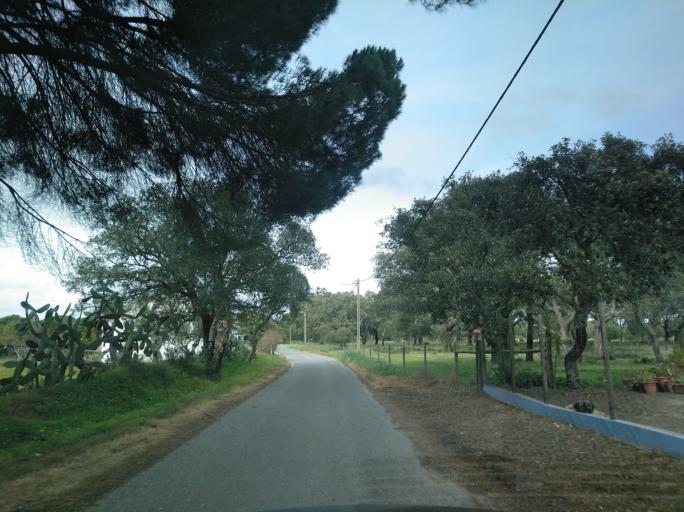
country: PT
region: Setubal
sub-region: Grandola
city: Grandola
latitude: 38.2000
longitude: -8.5458
